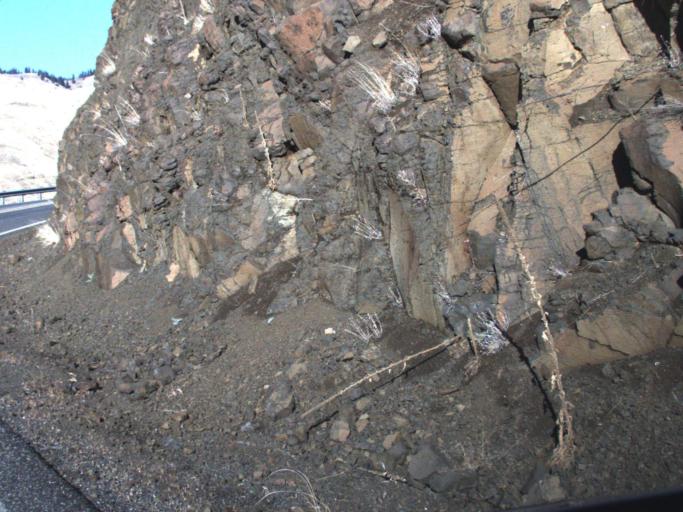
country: US
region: Washington
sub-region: Asotin County
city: Asotin
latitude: 46.0625
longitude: -117.2324
